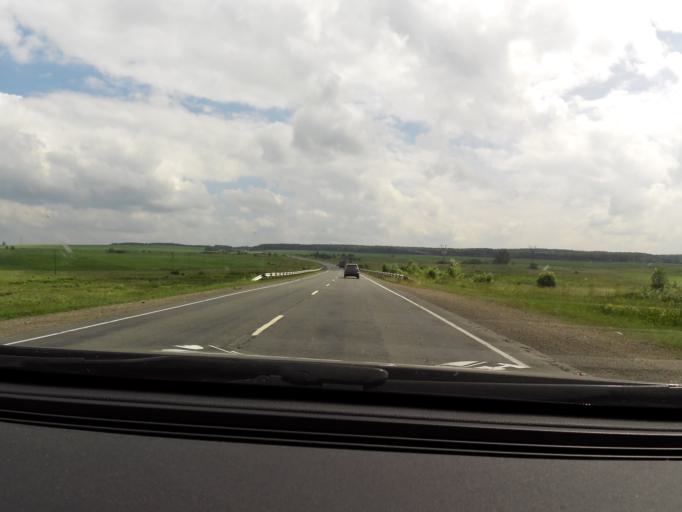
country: RU
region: Sverdlovsk
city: Achit
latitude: 56.8906
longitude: 57.6087
